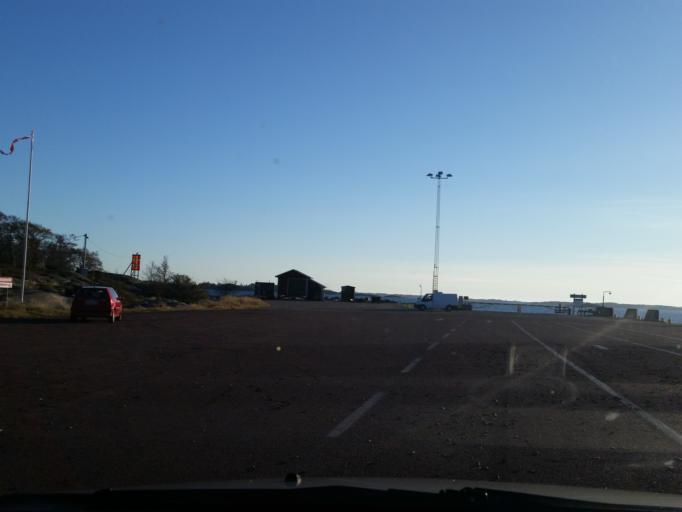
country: AX
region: Alands skaergard
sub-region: Braendoe
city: Braendoe
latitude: 60.3576
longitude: 21.0382
